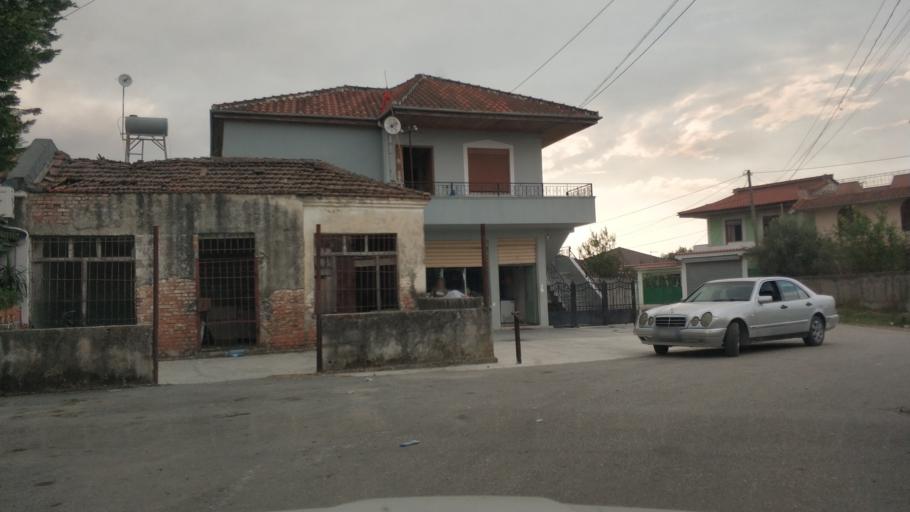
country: AL
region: Fier
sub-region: Rrethi i Fierit
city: Dermenas
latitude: 40.7300
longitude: 19.4677
